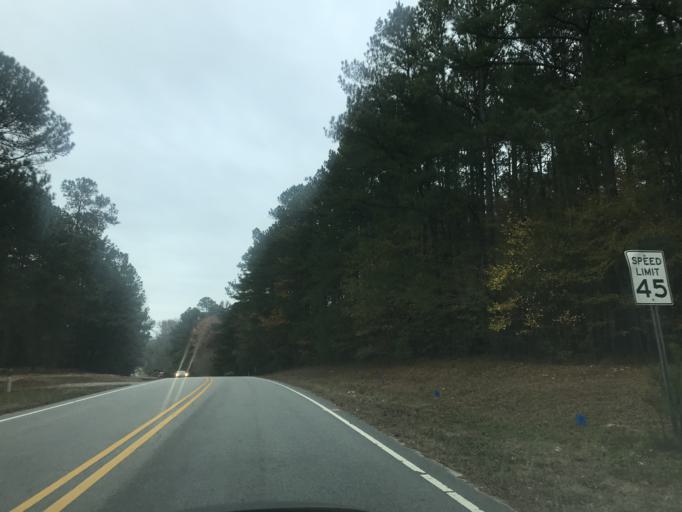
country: US
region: North Carolina
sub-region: Wake County
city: Wake Forest
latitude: 35.9981
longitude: -78.4973
